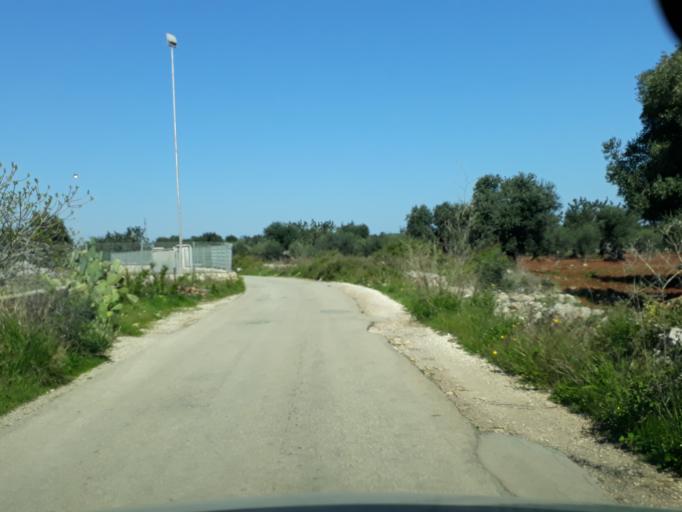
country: IT
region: Apulia
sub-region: Provincia di Brindisi
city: Fasano
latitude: 40.8287
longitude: 17.3814
